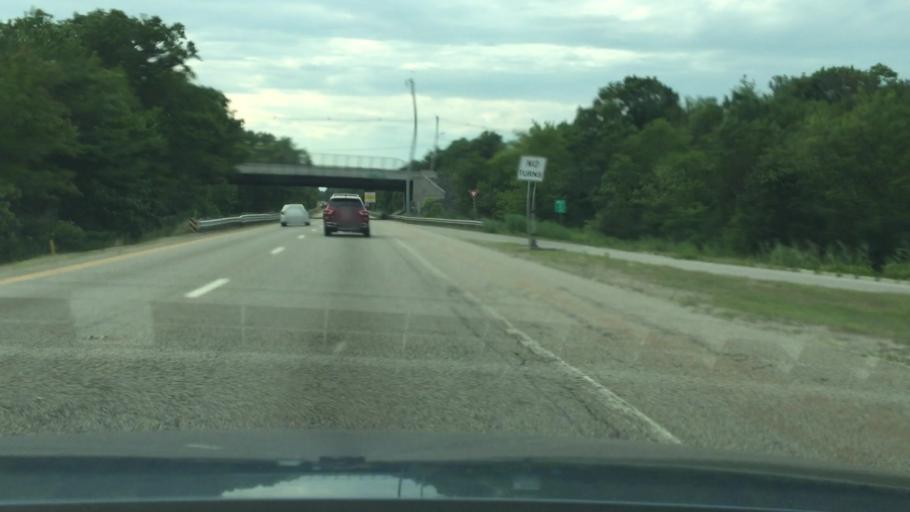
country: US
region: Massachusetts
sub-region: Plymouth County
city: Hanover
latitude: 42.1507
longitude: -70.8441
